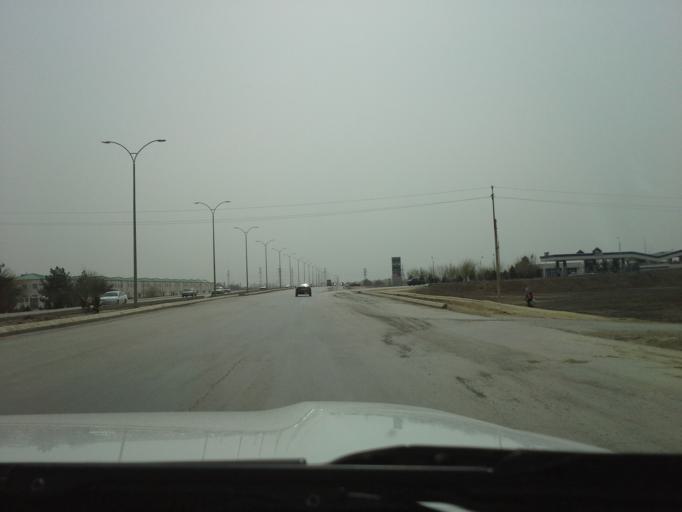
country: TM
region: Ahal
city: Tejen
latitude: 37.3743
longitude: 60.5186
